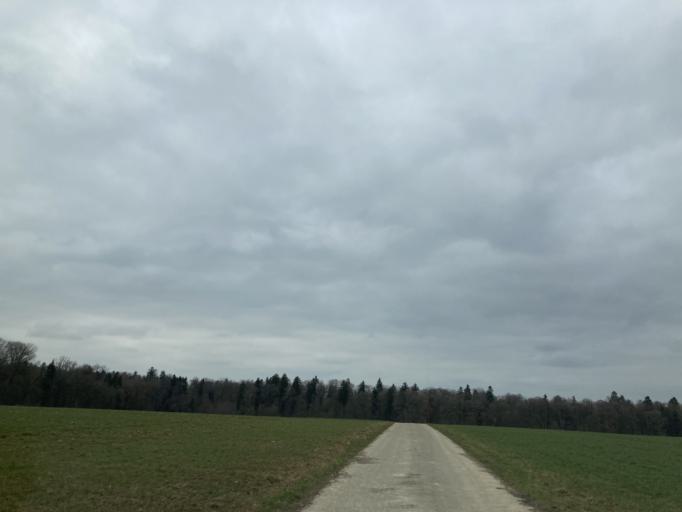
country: DE
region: Baden-Wuerttemberg
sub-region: Tuebingen Region
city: Hirrlingen
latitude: 48.4341
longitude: 8.8996
